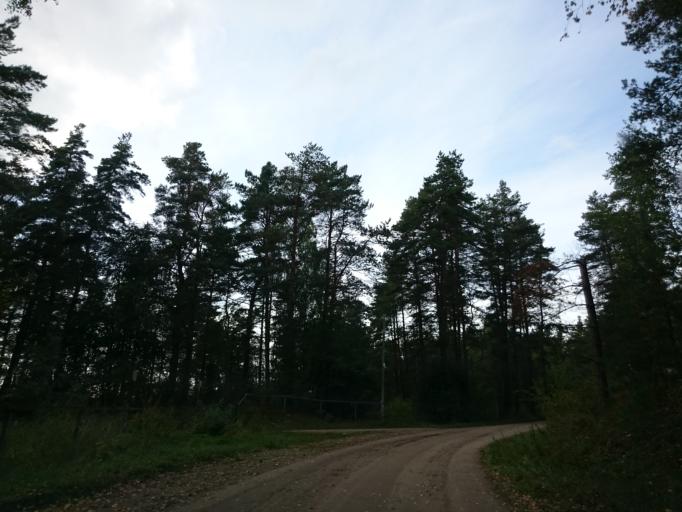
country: LV
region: Garkalne
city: Garkalne
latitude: 57.0477
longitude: 24.3825
